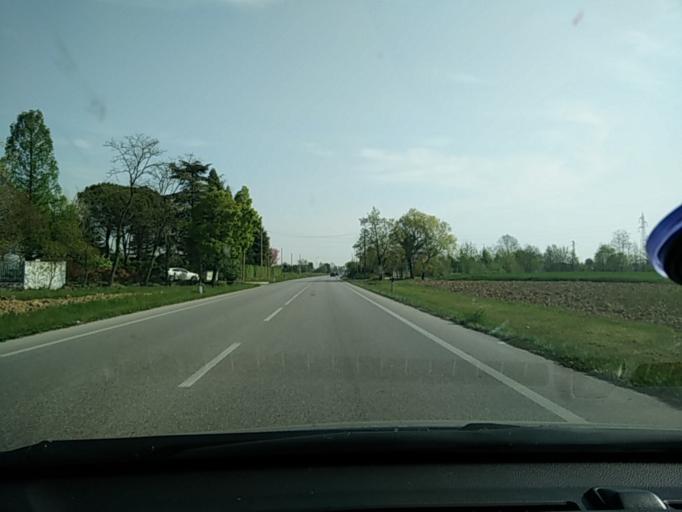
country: IT
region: Friuli Venezia Giulia
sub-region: Provincia di Pordenone
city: Azzano Decimo
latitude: 45.9183
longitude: 12.6325
